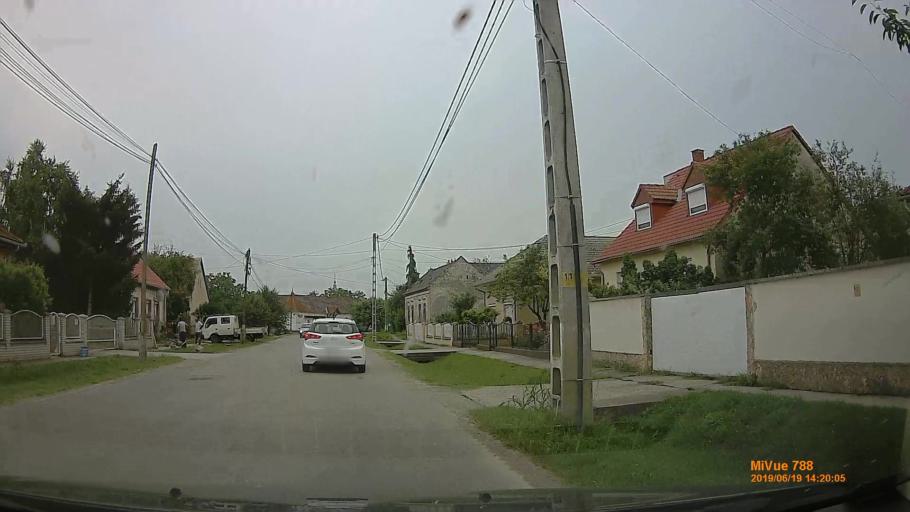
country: HU
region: Baranya
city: Szigetvar
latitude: 46.0273
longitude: 17.7785
